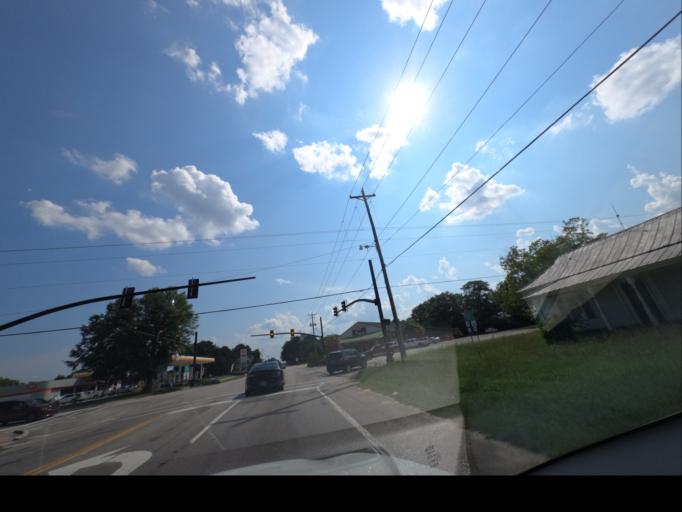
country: US
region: South Carolina
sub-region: Lexington County
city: Gaston
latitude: 33.7649
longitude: -81.2451
